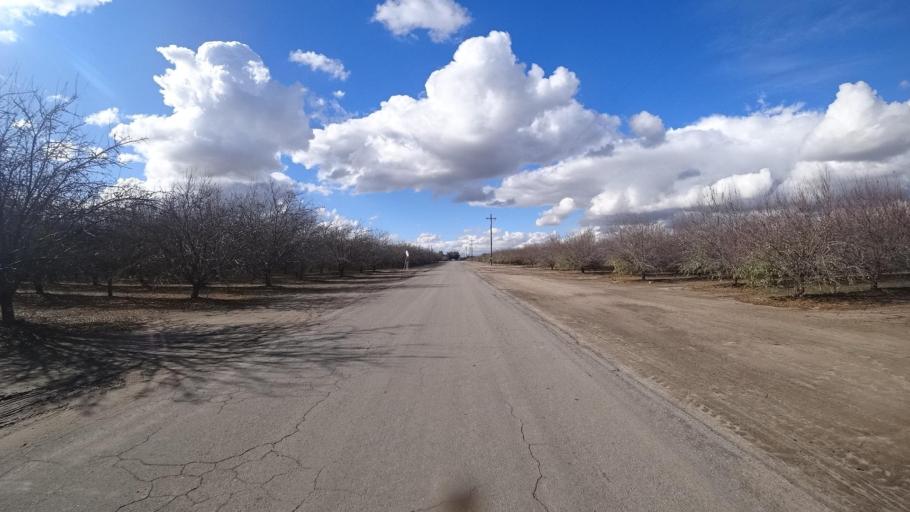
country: US
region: California
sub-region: Kern County
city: Greenfield
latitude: 35.2526
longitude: -119.0604
